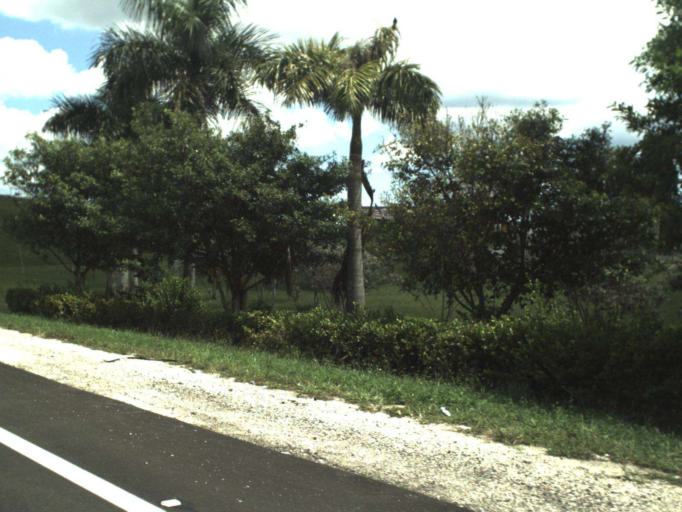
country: US
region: Florida
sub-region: Miami-Dade County
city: Golden Glades
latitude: 25.9257
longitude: -80.2078
